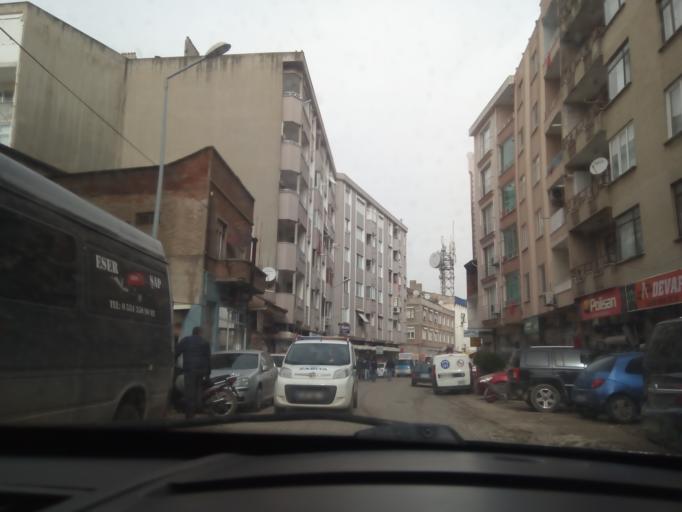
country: TR
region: Balikesir
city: Susurluk
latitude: 39.9131
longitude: 28.1570
